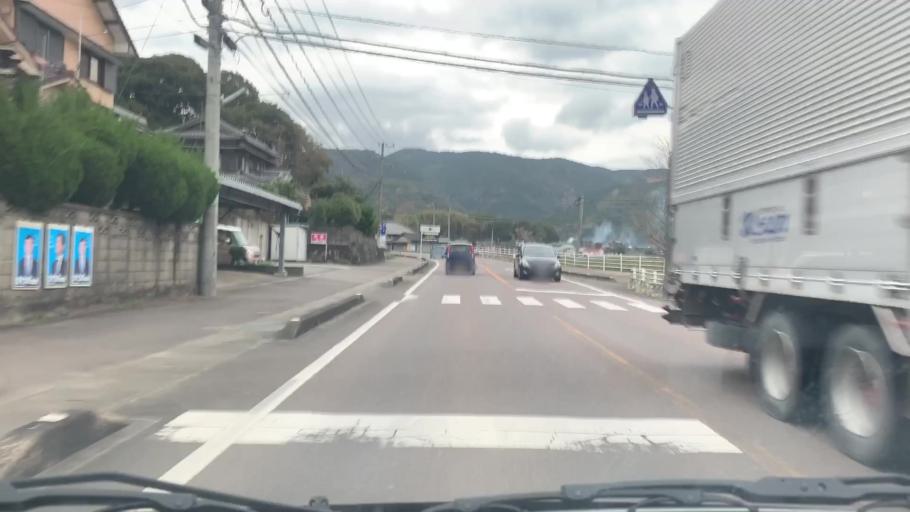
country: JP
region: Saga Prefecture
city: Kashima
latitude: 33.1509
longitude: 130.0643
